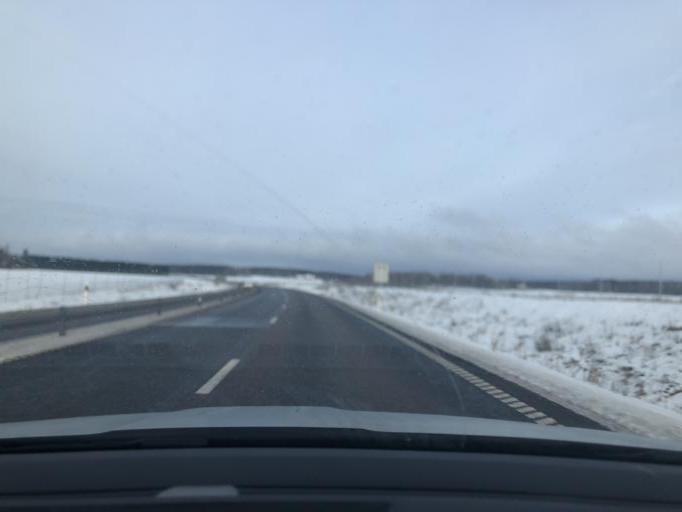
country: SE
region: OEstergoetland
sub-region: Motala Kommun
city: Borensberg
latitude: 58.5752
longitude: 15.2374
